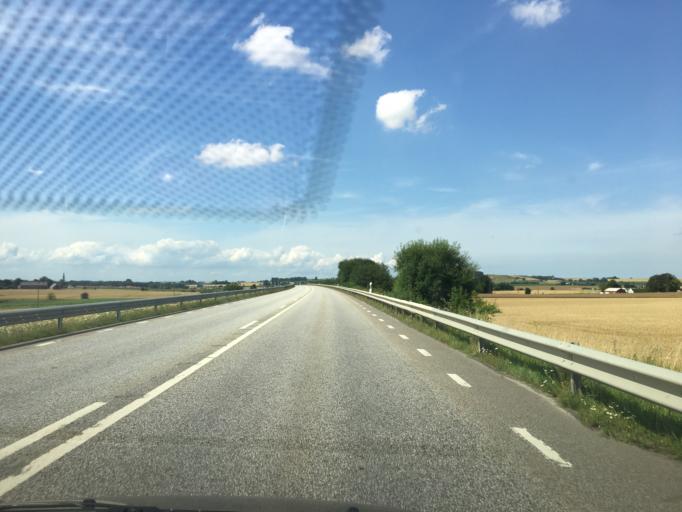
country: SE
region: Skane
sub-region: Landskrona
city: Asmundtorp
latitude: 55.8900
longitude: 12.9881
